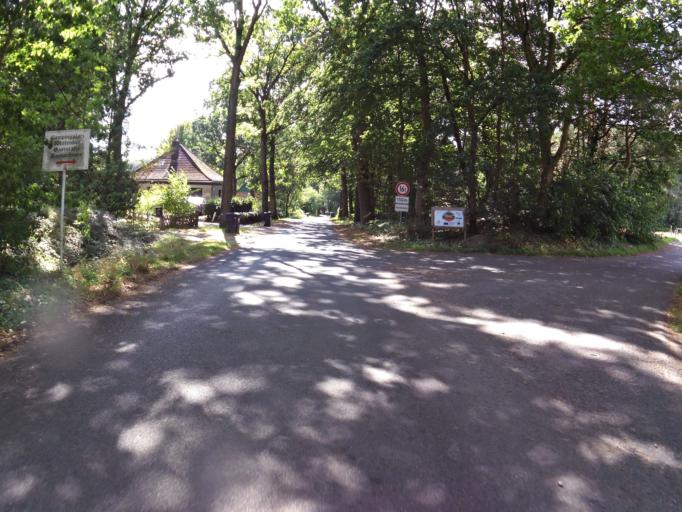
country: DE
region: Lower Saxony
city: Seedorf
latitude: 53.3362
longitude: 9.1997
